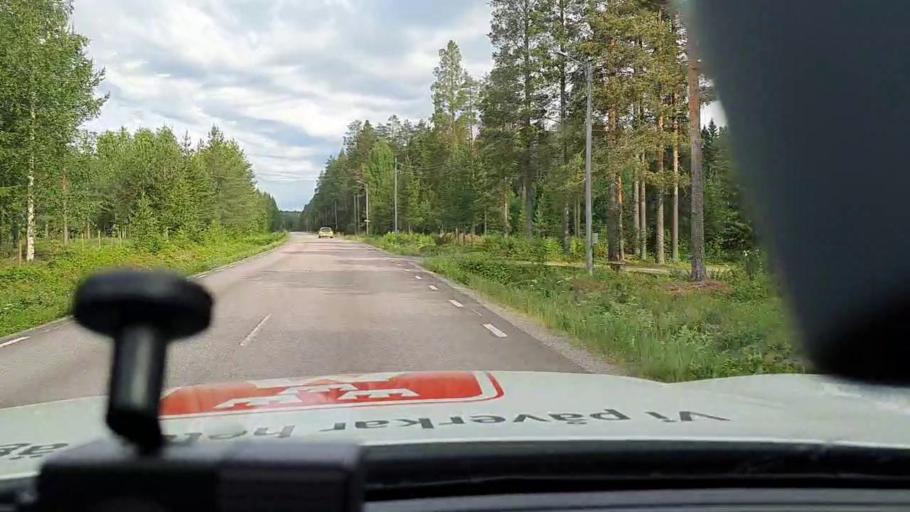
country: SE
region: Norrbotten
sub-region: Bodens Kommun
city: Saevast
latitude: 65.7252
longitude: 21.7491
